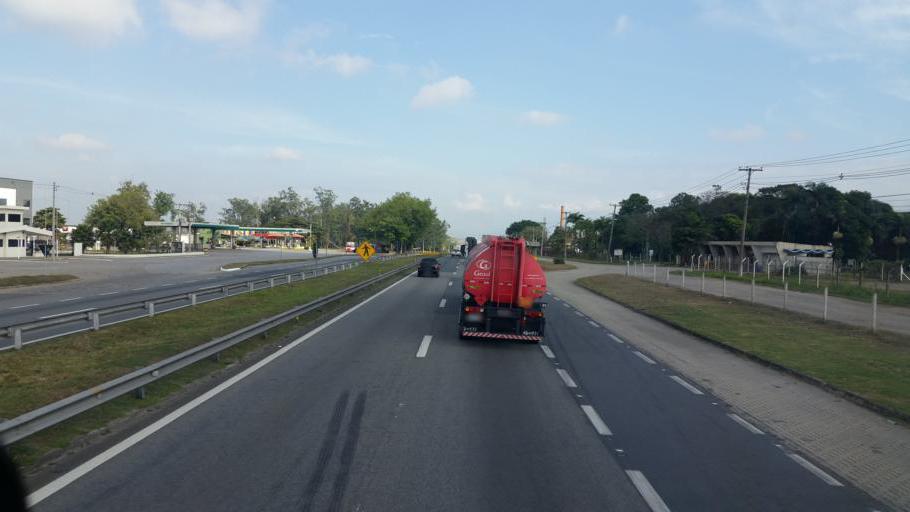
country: BR
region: Rio de Janeiro
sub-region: Resende
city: Resende
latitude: -22.4558
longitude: -44.3967
